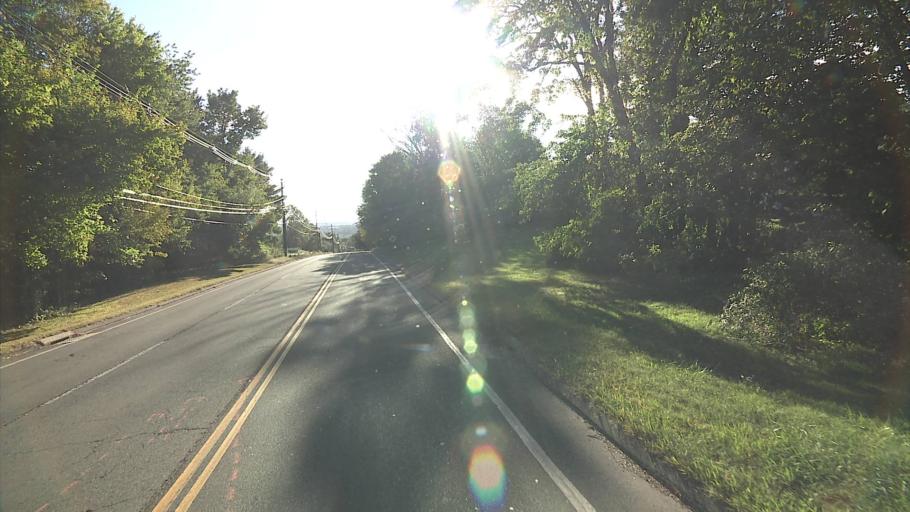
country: US
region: Connecticut
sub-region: New Haven County
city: Wallingford
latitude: 41.4930
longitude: -72.8351
